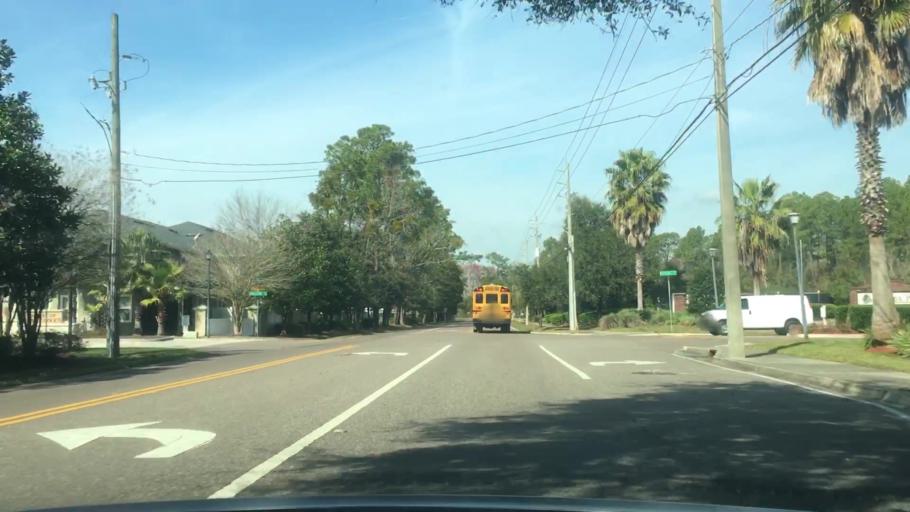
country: US
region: Florida
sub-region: Duval County
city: Jacksonville
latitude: 30.4605
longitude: -81.5605
